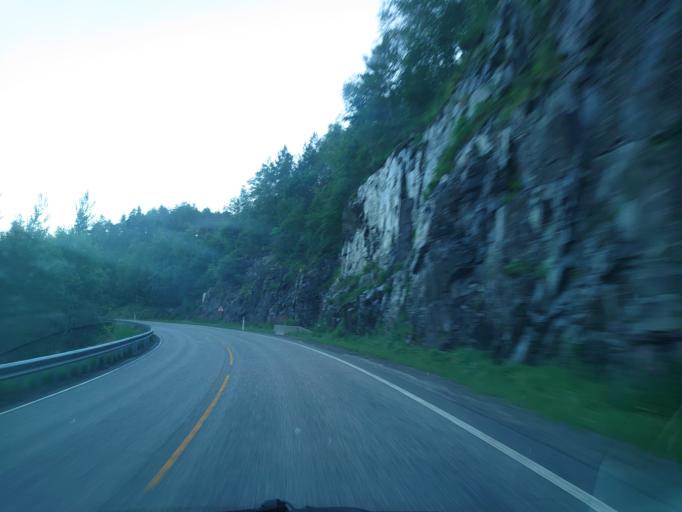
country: NO
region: Hordaland
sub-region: Osteroy
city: Lonevag
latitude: 60.6420
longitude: 5.4925
